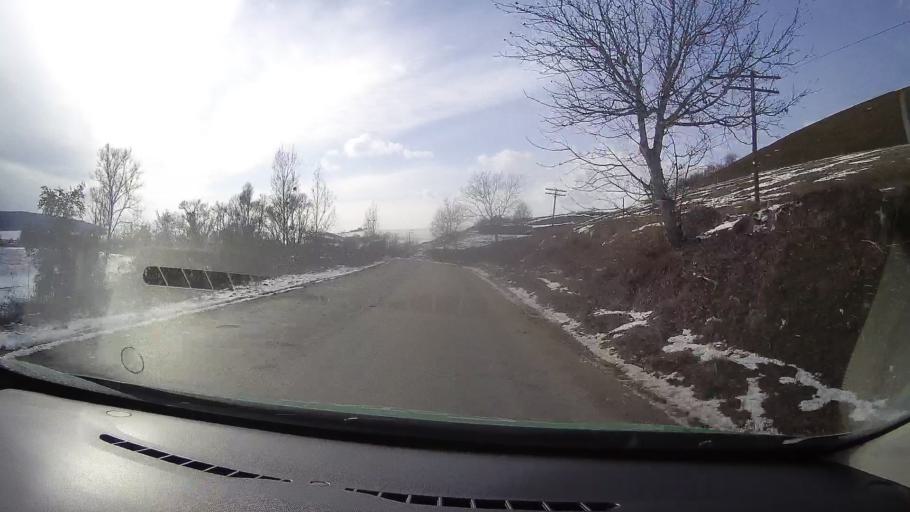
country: RO
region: Sibiu
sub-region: Comuna Iacobeni
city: Iacobeni
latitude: 46.0416
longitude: 24.7368
